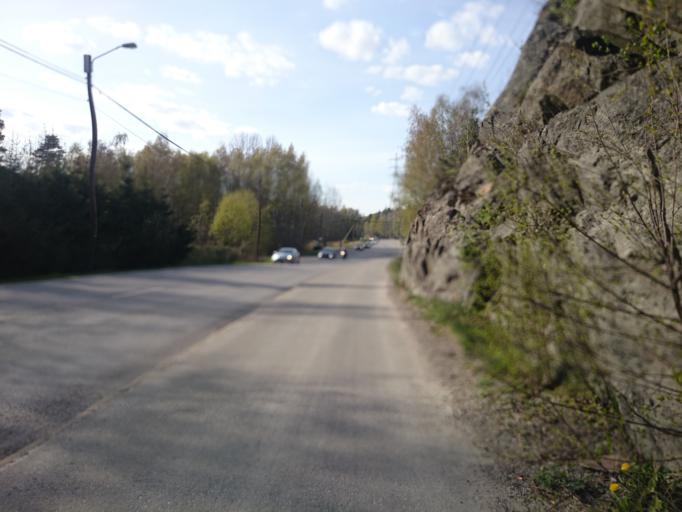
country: SE
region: Stockholm
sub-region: Huddinge Kommun
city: Huddinge
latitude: 59.2355
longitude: 18.0372
